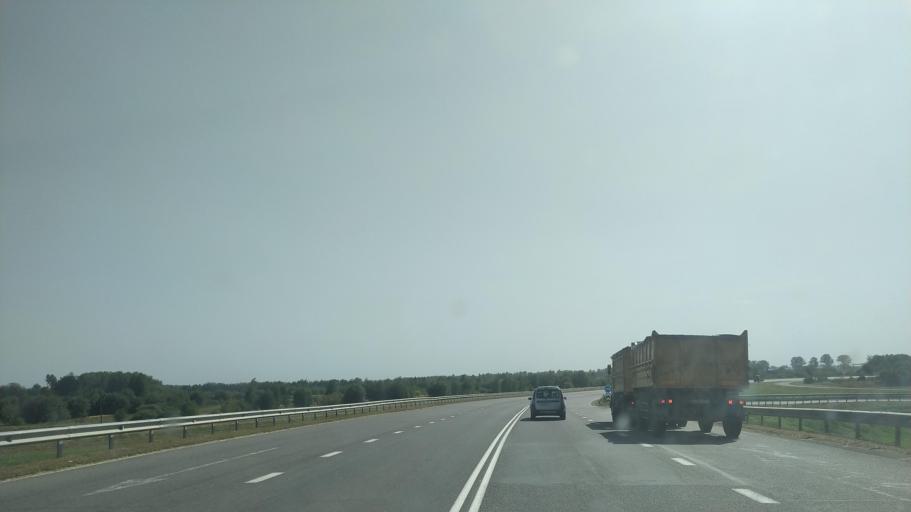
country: BY
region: Brest
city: Byaroza
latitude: 52.4892
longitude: 24.9689
